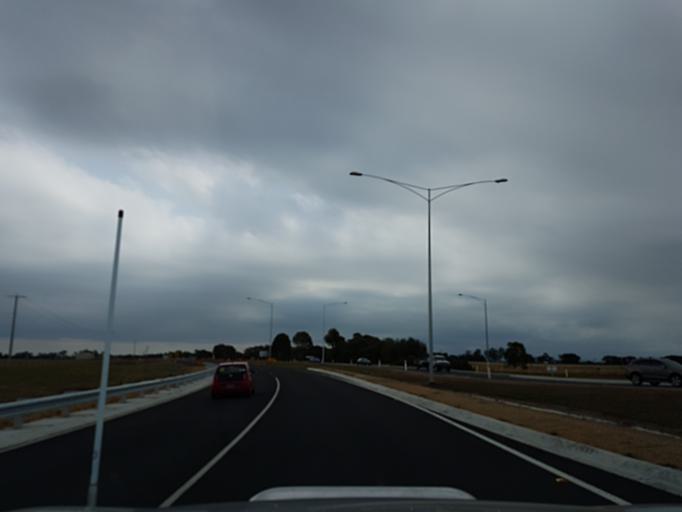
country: AU
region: Victoria
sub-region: Wellington
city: Sale
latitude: -38.1004
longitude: 146.9889
